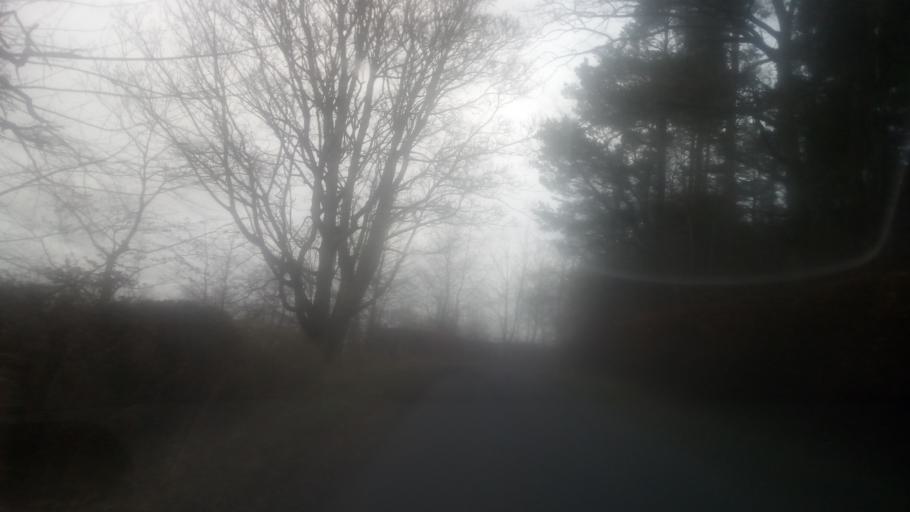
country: GB
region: Scotland
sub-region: The Scottish Borders
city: Jedburgh
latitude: 55.4806
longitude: -2.5250
